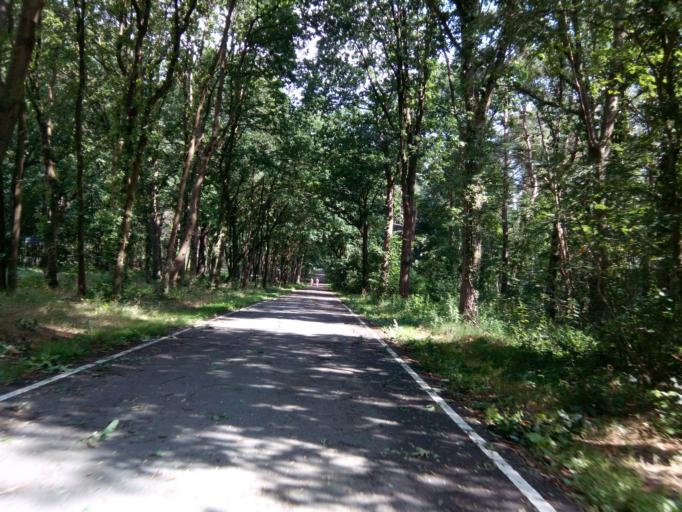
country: NL
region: Utrecht
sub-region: Gemeente Utrechtse Heuvelrug
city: Maarn
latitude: 52.0569
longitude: 5.3531
